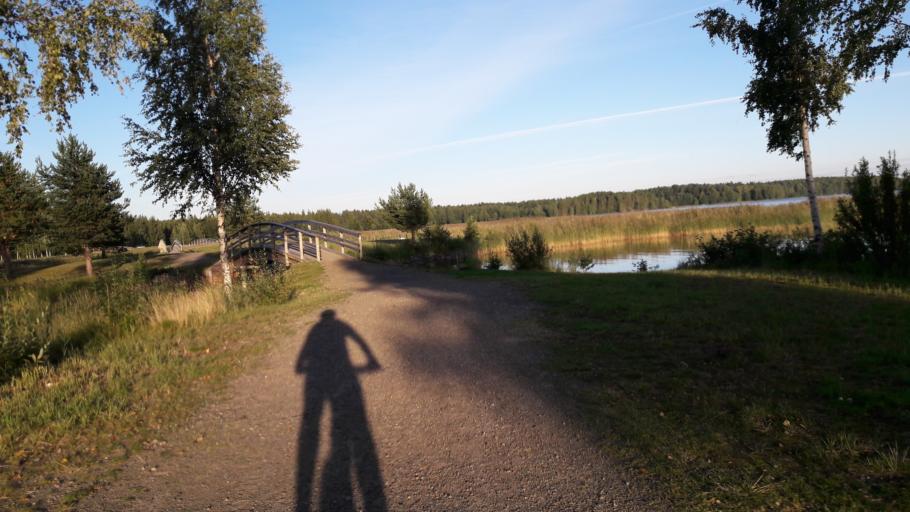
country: FI
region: North Karelia
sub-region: Joensuu
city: Joensuu
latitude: 62.6131
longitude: 29.7006
